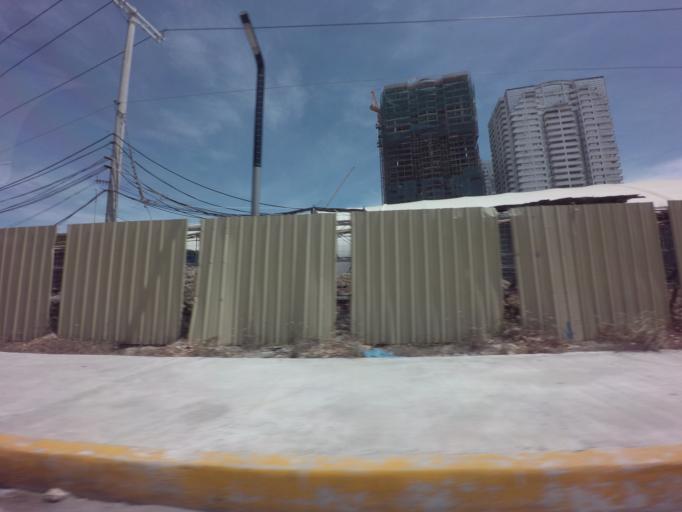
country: PH
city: Sambayanihan People's Village
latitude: 14.5121
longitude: 120.9792
